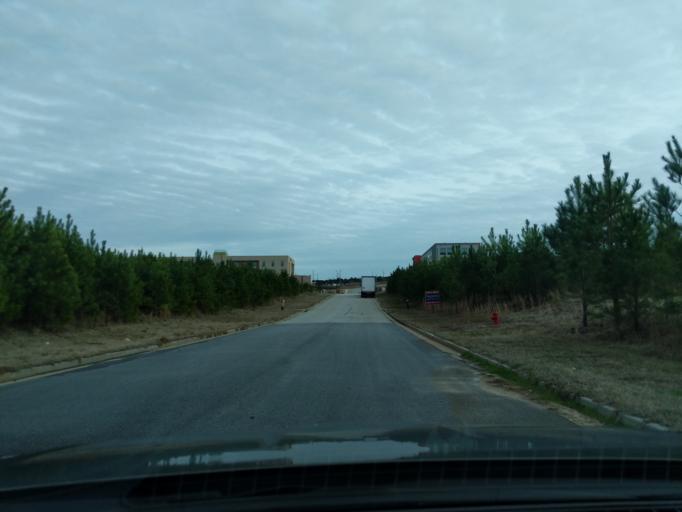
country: US
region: Georgia
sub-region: Columbia County
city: Grovetown
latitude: 33.4824
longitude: -82.2023
